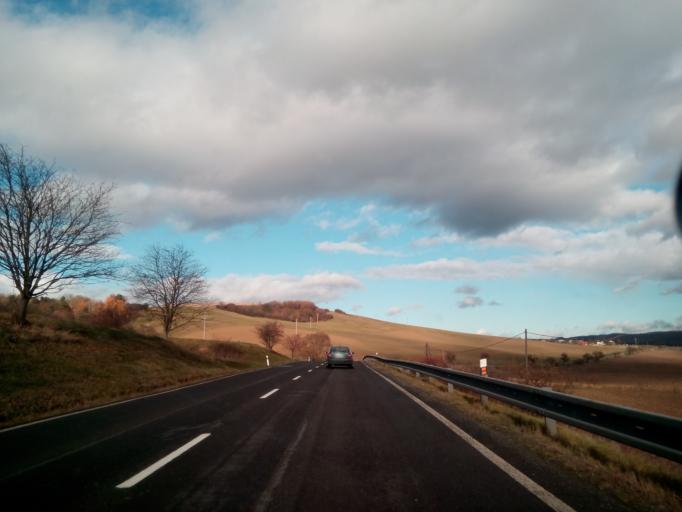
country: SK
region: Presovsky
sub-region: Okres Bardejov
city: Bardejov
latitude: 49.1754
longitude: 21.3065
